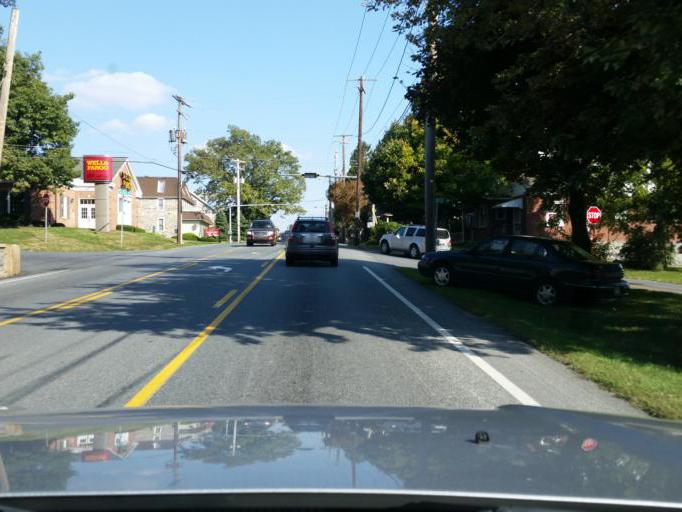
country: US
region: Pennsylvania
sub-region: Lancaster County
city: Paradise
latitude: 40.0098
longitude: -76.1289
